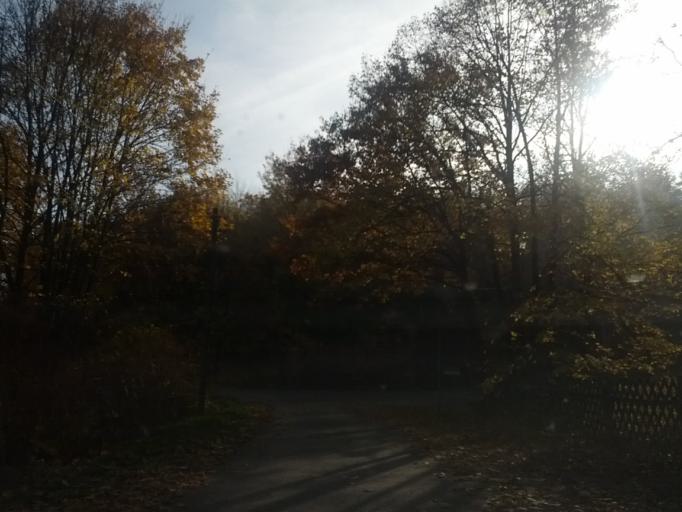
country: DE
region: Thuringia
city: Eisenach
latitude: 50.9377
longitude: 10.3409
